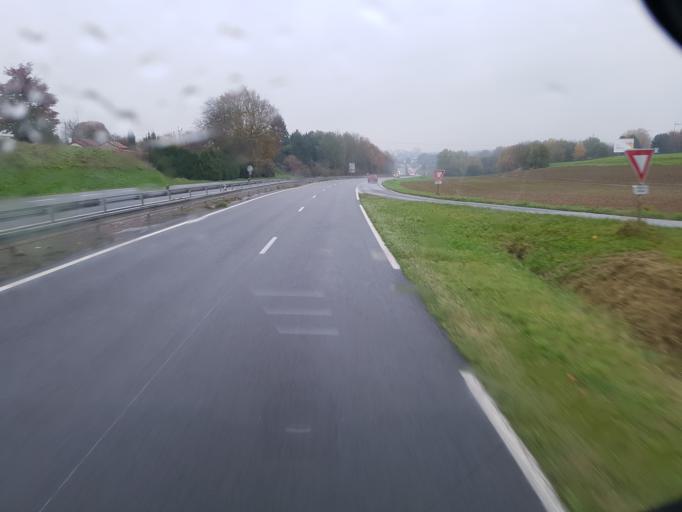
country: FR
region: Picardie
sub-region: Departement de l'Aisne
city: Gauchy
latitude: 49.8202
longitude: 3.2950
